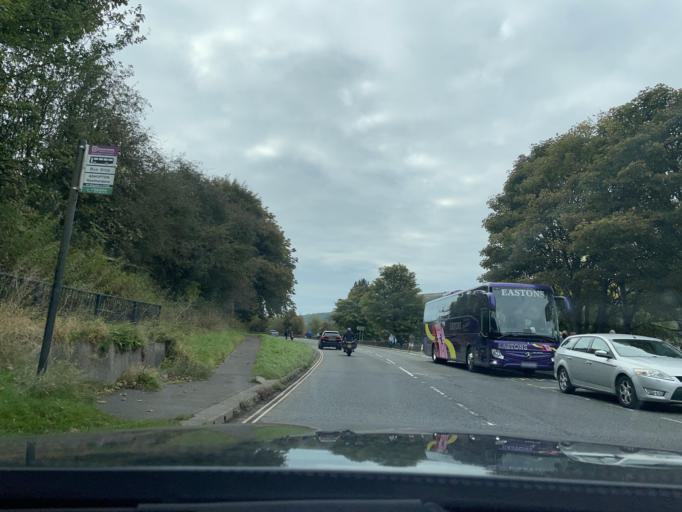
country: GB
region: England
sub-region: Derbyshire
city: Hope Valley
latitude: 53.3708
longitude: -1.6974
